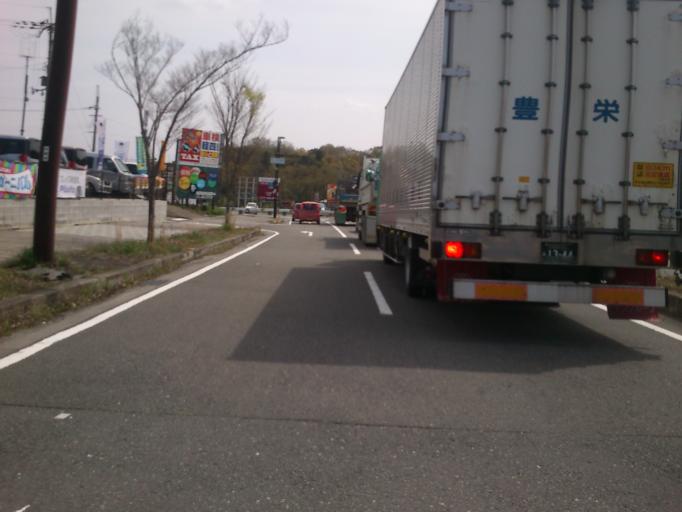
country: JP
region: Nara
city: Nara-shi
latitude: 34.7518
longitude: 135.7884
